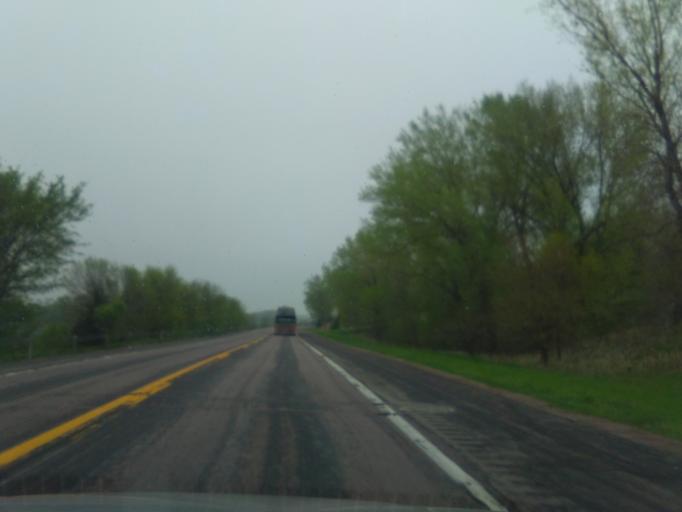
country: US
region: Nebraska
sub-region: Burt County
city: Oakland
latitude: 41.7980
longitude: -96.4829
